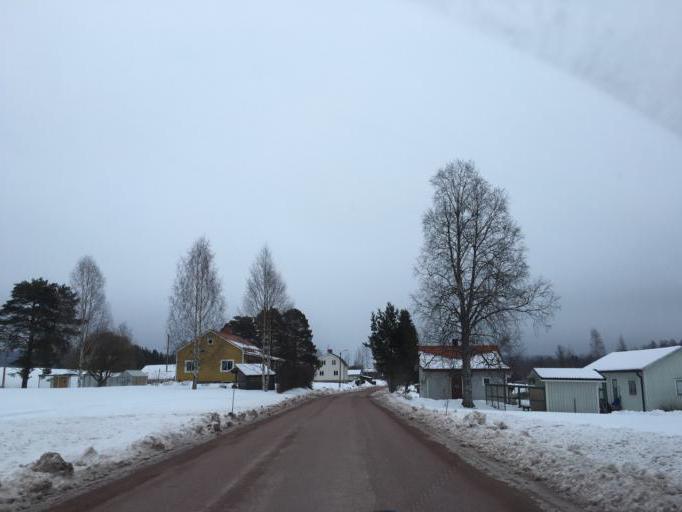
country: SE
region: Dalarna
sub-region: Alvdalens Kommun
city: AElvdalen
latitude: 61.2575
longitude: 14.0486
